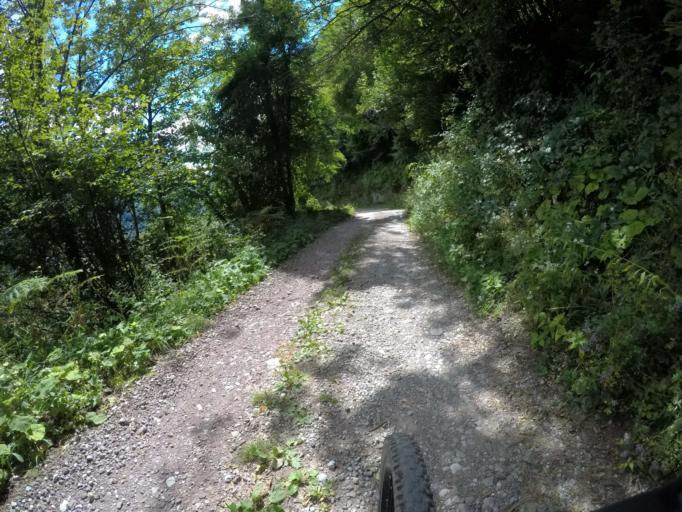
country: IT
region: Friuli Venezia Giulia
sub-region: Provincia di Udine
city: Zuglio
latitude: 46.4701
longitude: 13.0491
